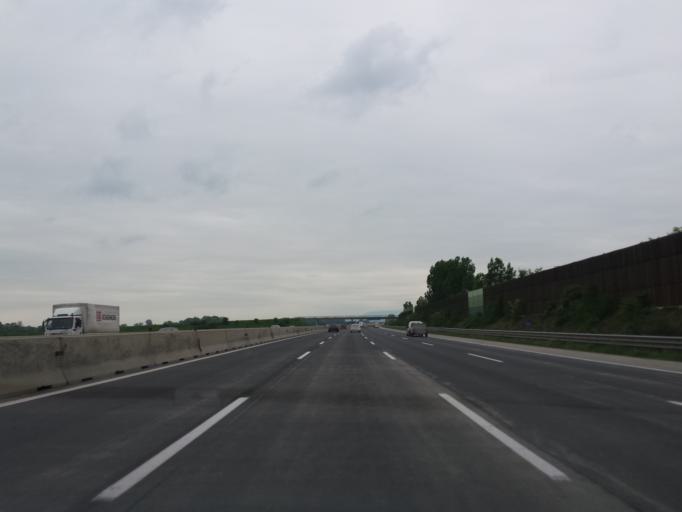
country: AT
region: Lower Austria
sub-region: Politischer Bezirk Baden
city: Trumau
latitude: 48.0167
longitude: 16.3241
